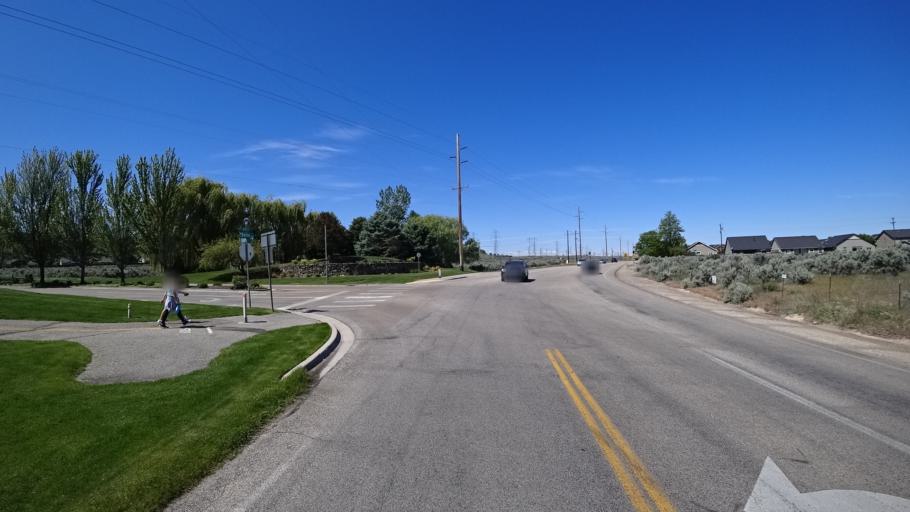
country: US
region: Idaho
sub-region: Ada County
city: Boise
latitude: 43.5604
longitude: -116.1327
